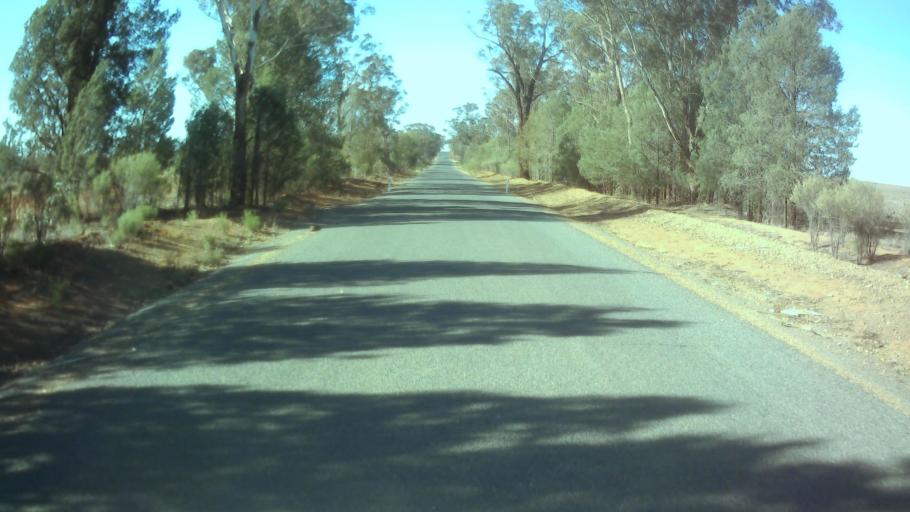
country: AU
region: New South Wales
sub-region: Forbes
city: Forbes
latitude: -33.7108
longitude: 147.8047
